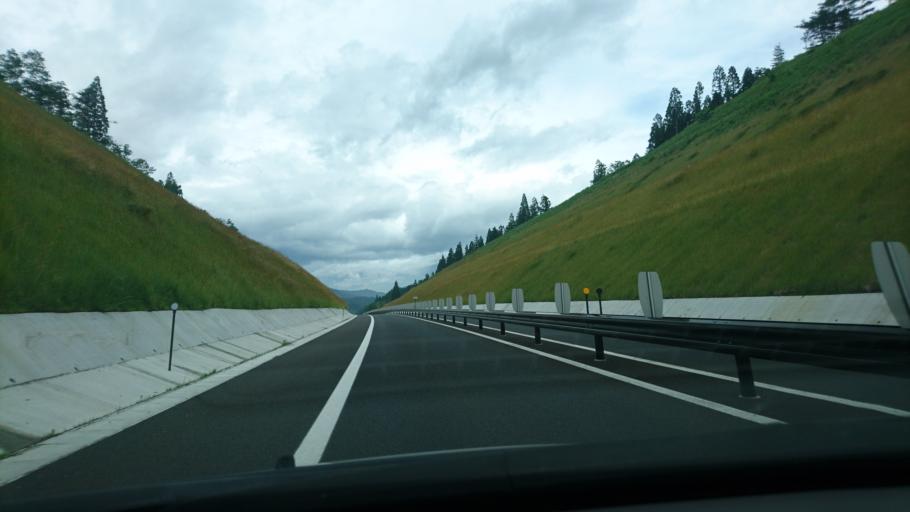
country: JP
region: Iwate
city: Yamada
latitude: 39.5510
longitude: 141.9257
